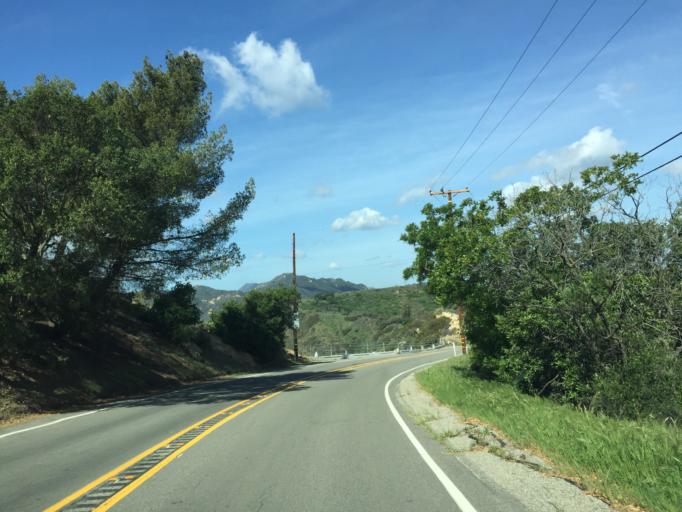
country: US
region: California
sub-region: Los Angeles County
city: Malibu Beach
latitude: 34.0686
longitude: -118.6893
